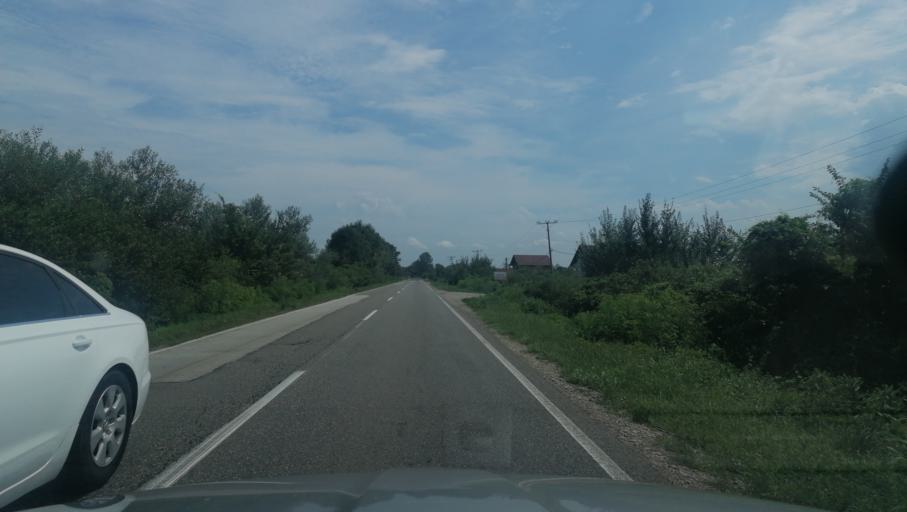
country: BA
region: Republika Srpska
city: Bosanski Samac
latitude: 45.0401
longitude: 18.4984
